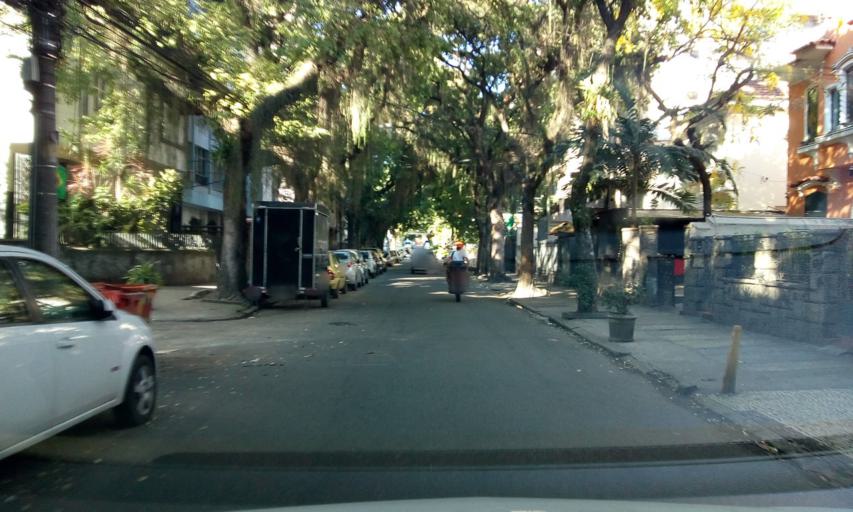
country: BR
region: Rio de Janeiro
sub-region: Rio De Janeiro
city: Rio de Janeiro
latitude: -22.9567
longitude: -43.1825
